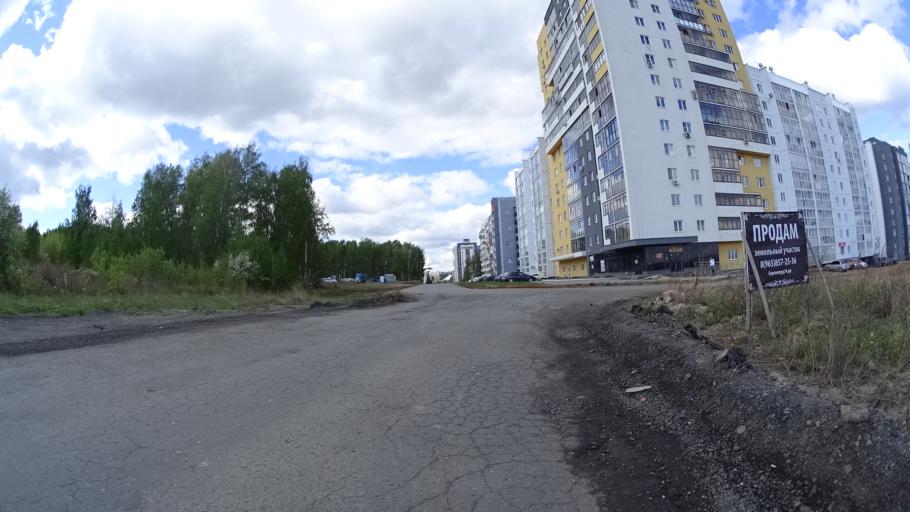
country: RU
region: Chelyabinsk
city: Sargazy
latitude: 55.1597
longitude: 61.2857
